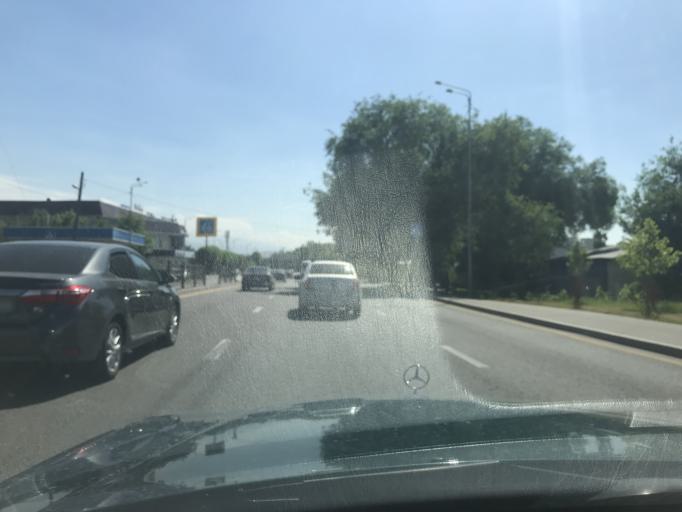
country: KZ
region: Almaty Qalasy
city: Almaty
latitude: 43.2922
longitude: 76.9929
